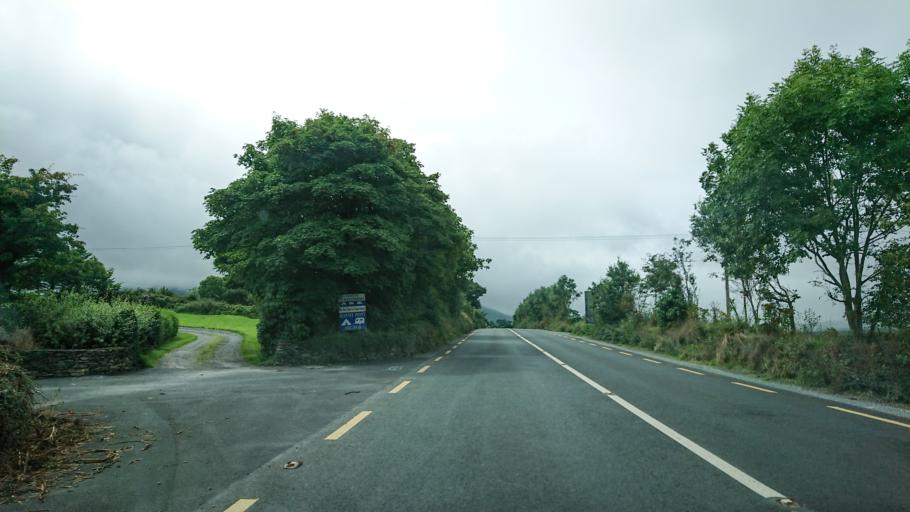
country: IE
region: Munster
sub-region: Ciarrai
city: Cahersiveen
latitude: 51.9653
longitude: -10.1738
